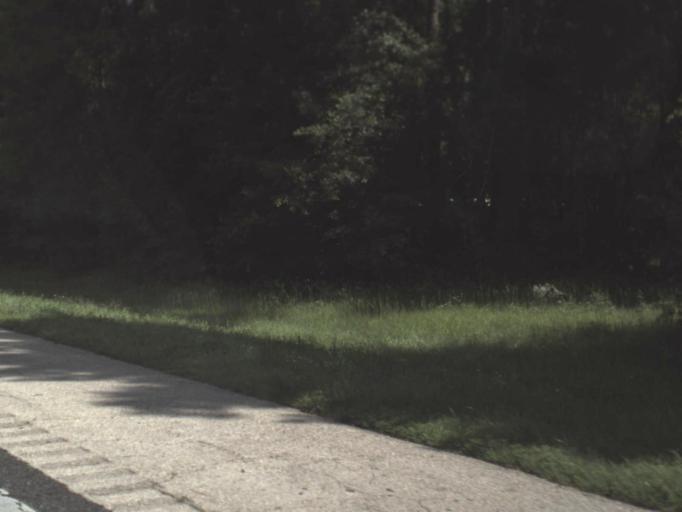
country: US
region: Florida
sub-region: Alachua County
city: High Springs
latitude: 29.8243
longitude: -82.5196
